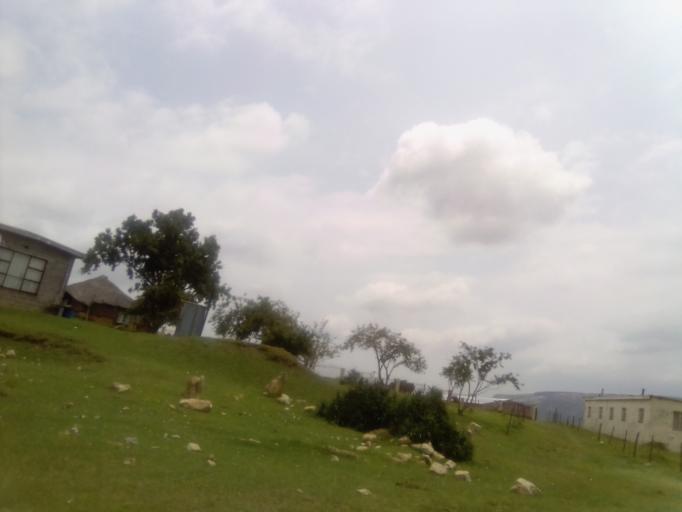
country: LS
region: Leribe
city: Leribe
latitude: -29.0386
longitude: 28.0188
